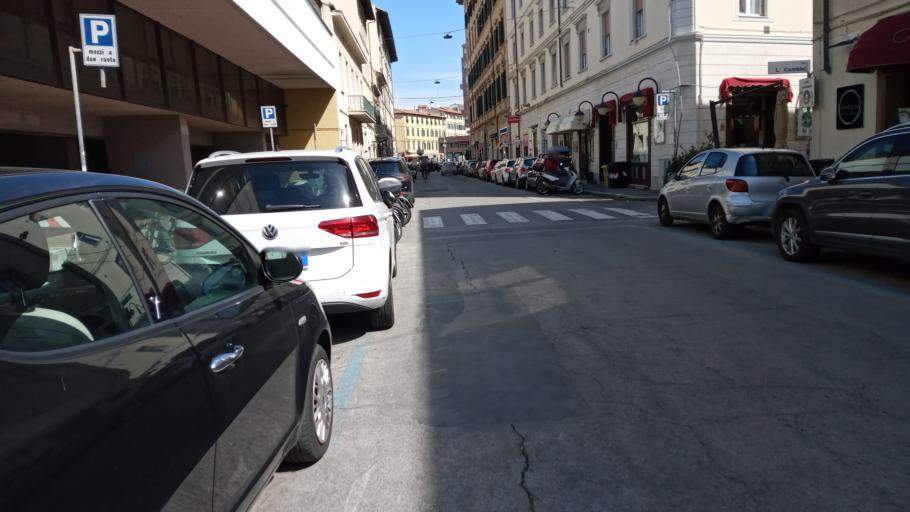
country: IT
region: Tuscany
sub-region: Provincia di Livorno
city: Livorno
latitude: 43.5428
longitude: 10.3134
